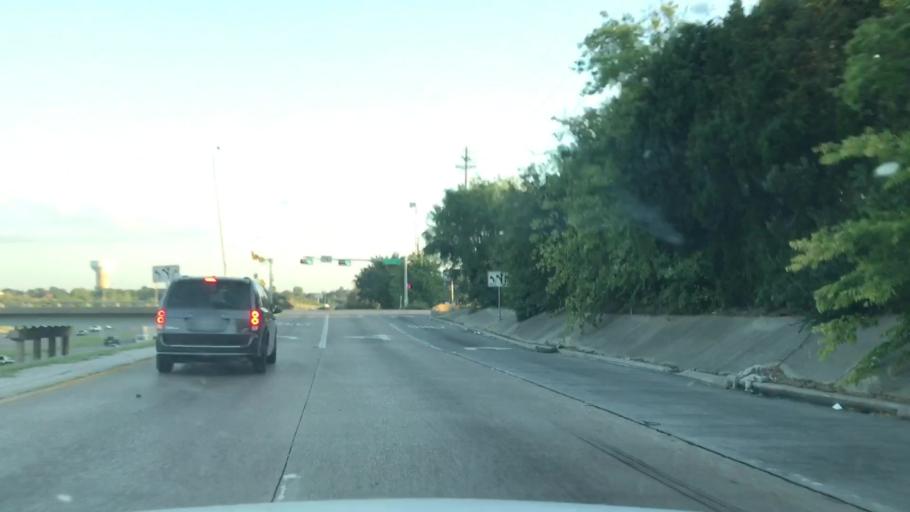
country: US
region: Texas
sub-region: Dallas County
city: Balch Springs
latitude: 32.7492
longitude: -96.6148
